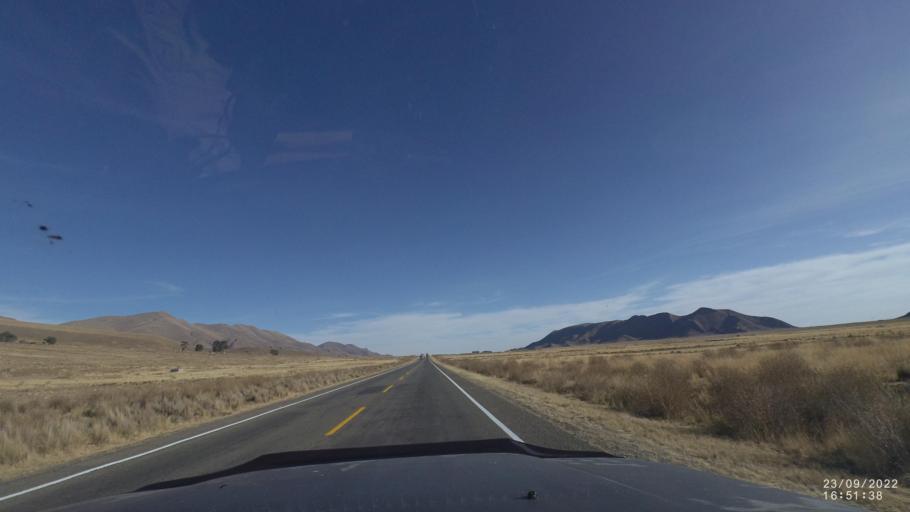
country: BO
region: Oruro
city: Poopo
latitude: -18.4183
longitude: -66.9752
